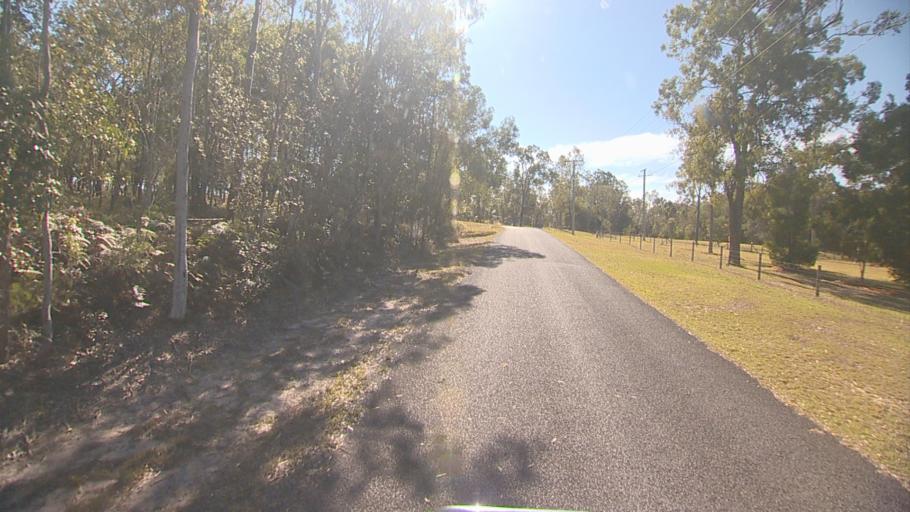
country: AU
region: Queensland
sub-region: Ipswich
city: Springfield Lakes
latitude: -27.7224
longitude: 152.9400
